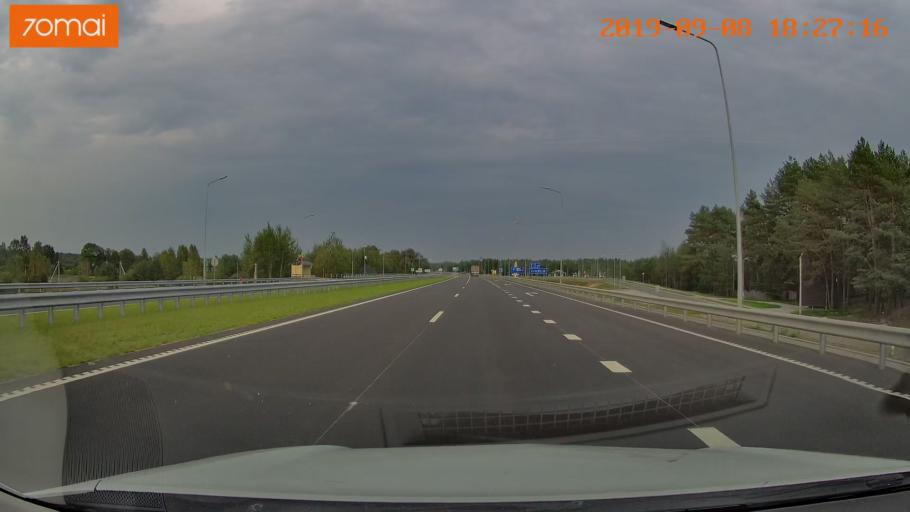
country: BY
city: Berezovka
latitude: 53.8454
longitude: 25.5995
